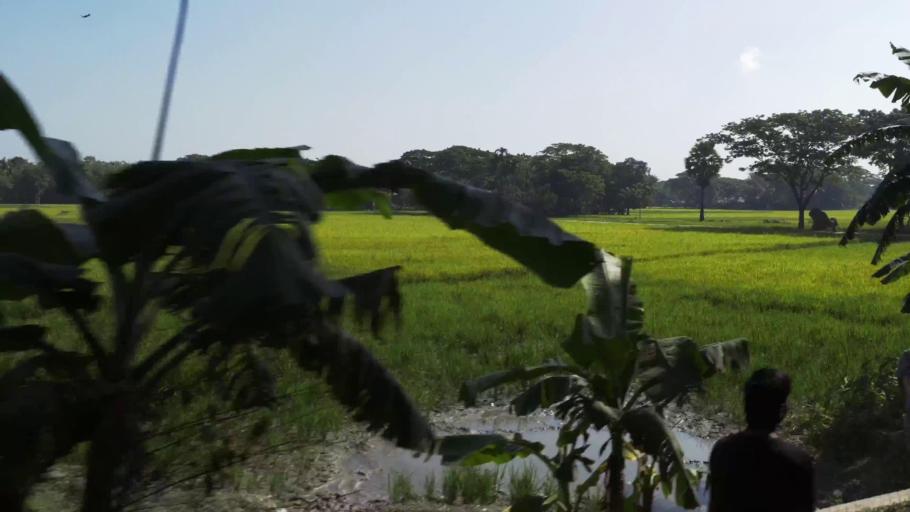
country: BD
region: Dhaka
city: Gafargaon
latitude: 24.5223
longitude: 90.5089
